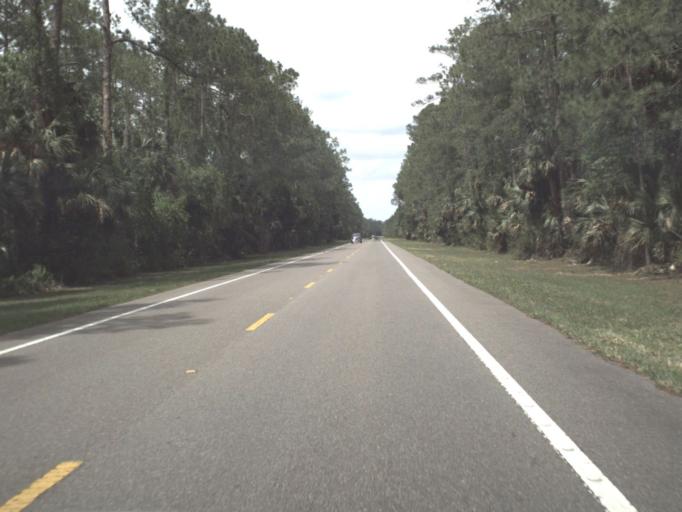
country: US
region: Florida
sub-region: Flagler County
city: Bunnell
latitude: 29.4019
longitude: -81.3067
